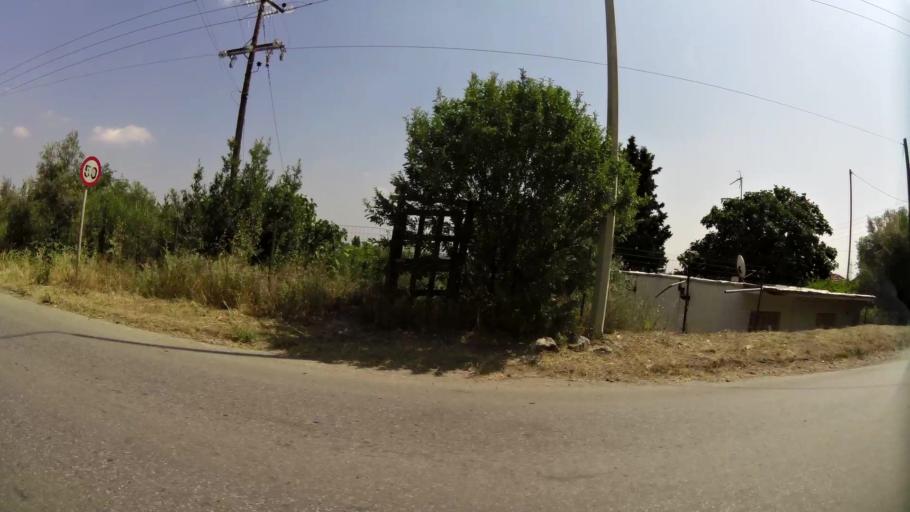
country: GR
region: Central Macedonia
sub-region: Nomos Imathias
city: Veroia
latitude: 40.5117
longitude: 22.2157
